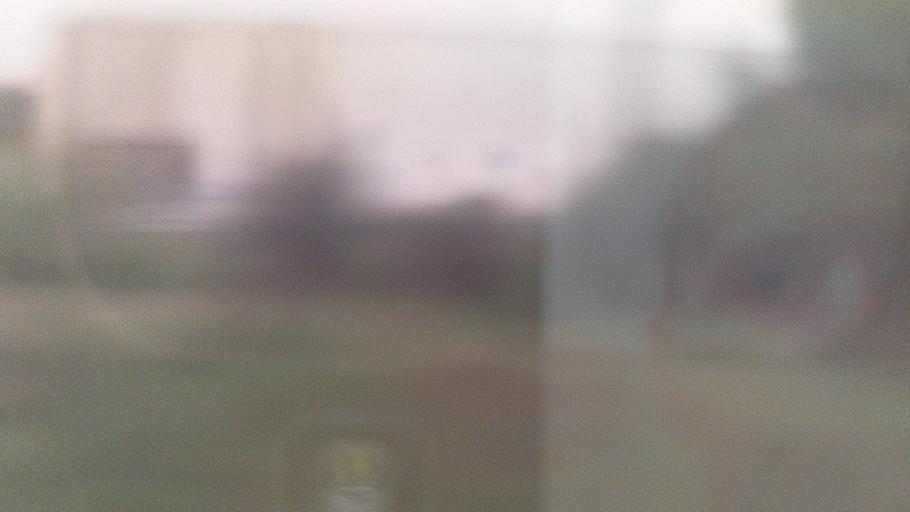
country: PT
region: Santarem
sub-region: Entroncamento
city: Entroncamento
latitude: 39.4770
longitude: -8.4651
